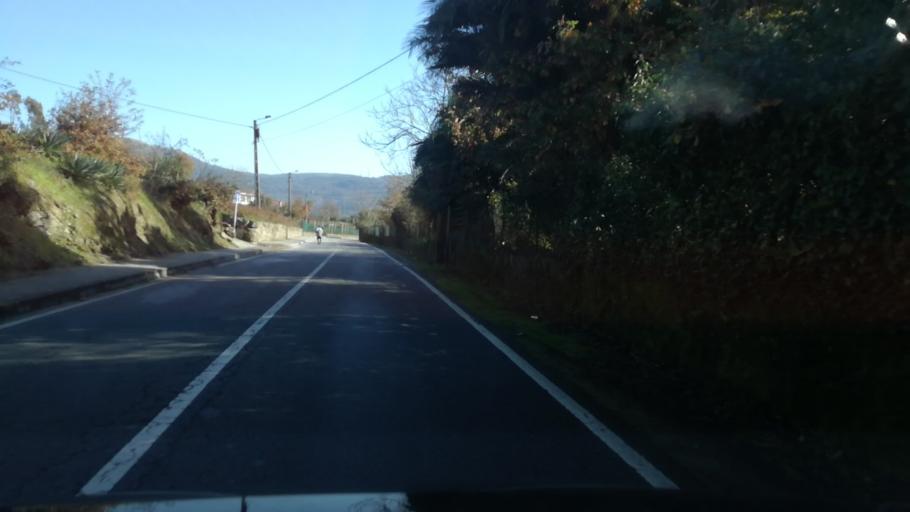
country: PT
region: Braga
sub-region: Guimaraes
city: Ponte
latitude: 41.5165
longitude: -8.3153
